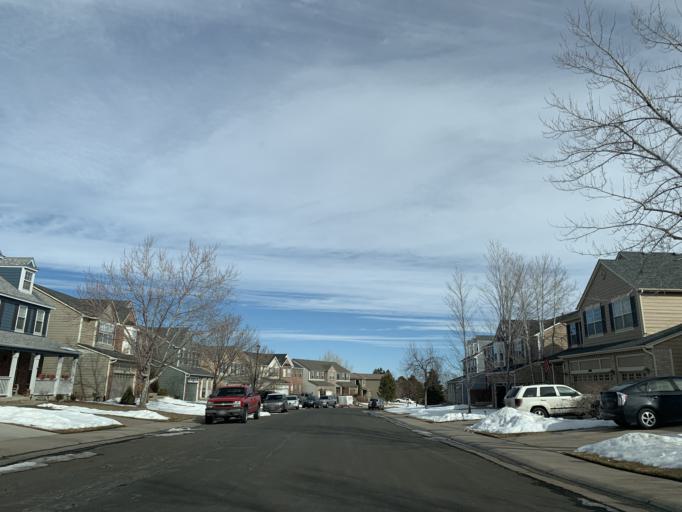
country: US
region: Colorado
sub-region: Douglas County
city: Carriage Club
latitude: 39.5345
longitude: -104.9368
